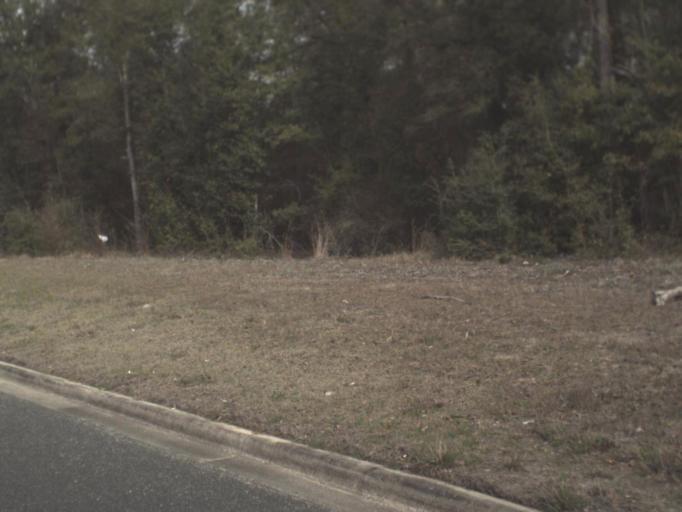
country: US
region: Florida
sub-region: Gadsden County
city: Midway
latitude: 30.4693
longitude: -84.4019
